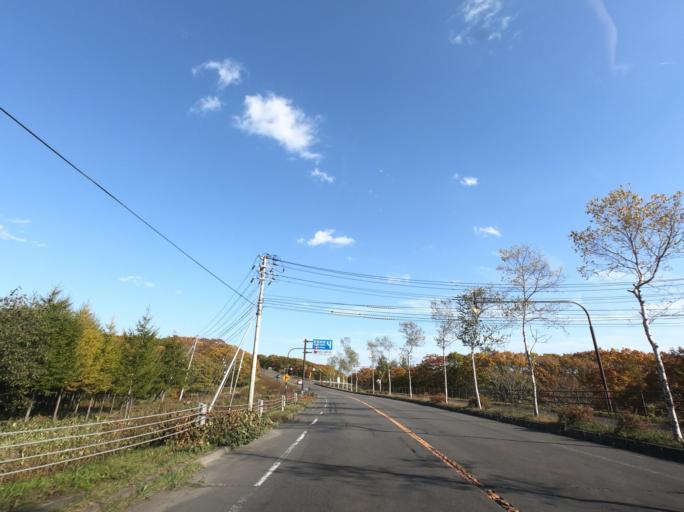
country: JP
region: Hokkaido
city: Kushiro
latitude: 43.0685
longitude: 144.3129
